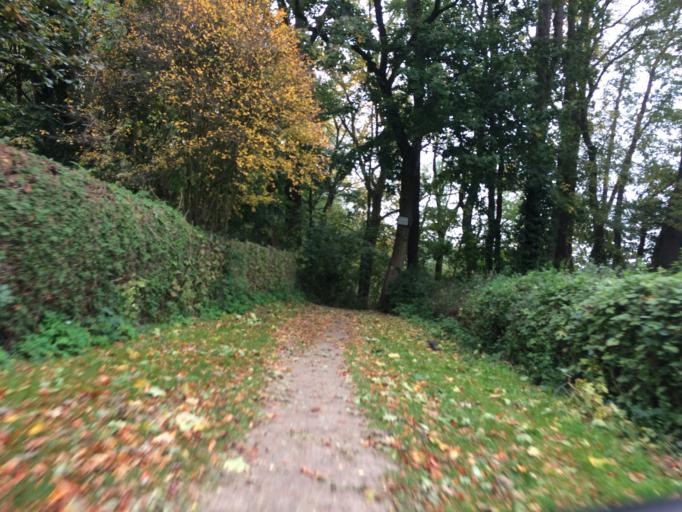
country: DE
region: Brandenburg
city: Glienicke
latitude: 52.6910
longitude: 13.3710
